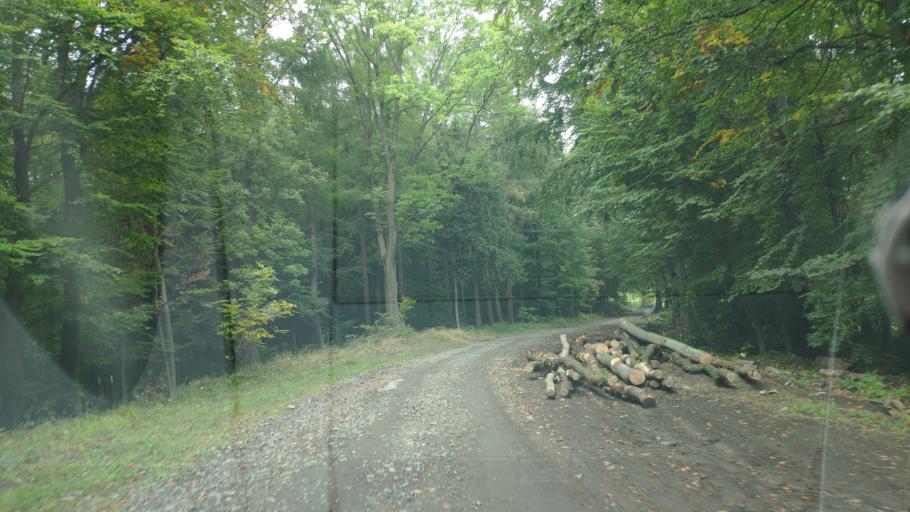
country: SK
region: Presovsky
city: Giraltovce
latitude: 48.9085
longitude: 21.4642
